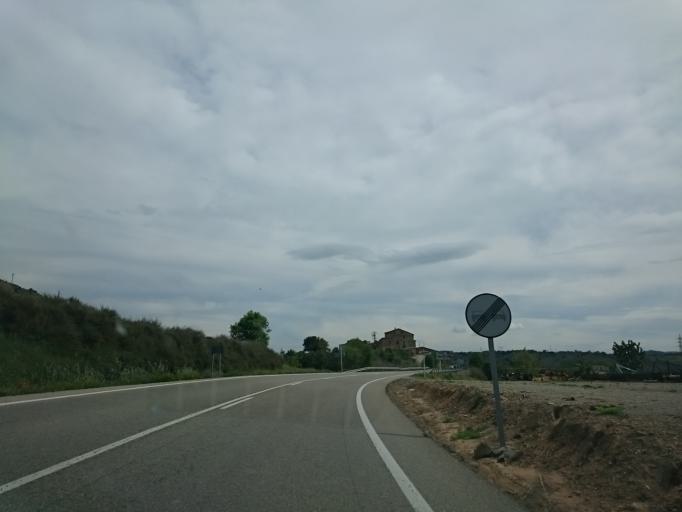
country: ES
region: Catalonia
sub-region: Provincia de Lleida
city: Tora de Riubregos
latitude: 41.8388
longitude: 1.3577
